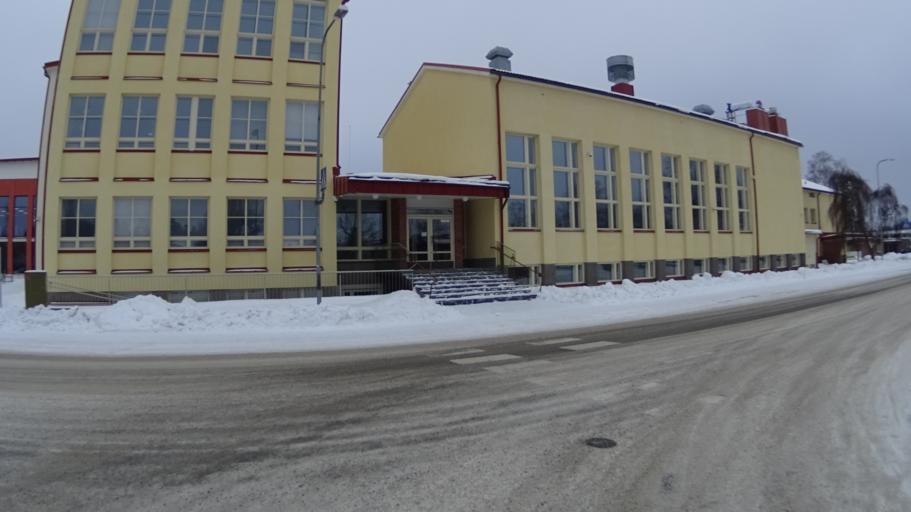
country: FI
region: Uusimaa
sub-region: Helsinki
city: Karkkila
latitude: 60.5352
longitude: 24.2137
